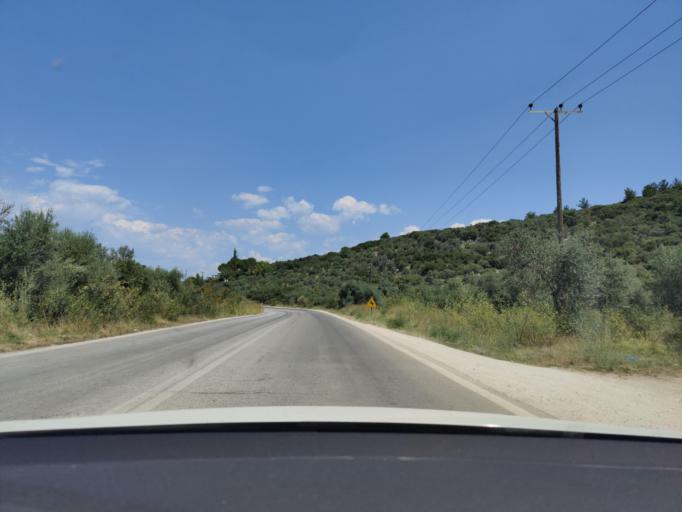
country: GR
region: East Macedonia and Thrace
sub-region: Nomos Kavalas
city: Prinos
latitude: 40.7638
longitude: 24.5965
